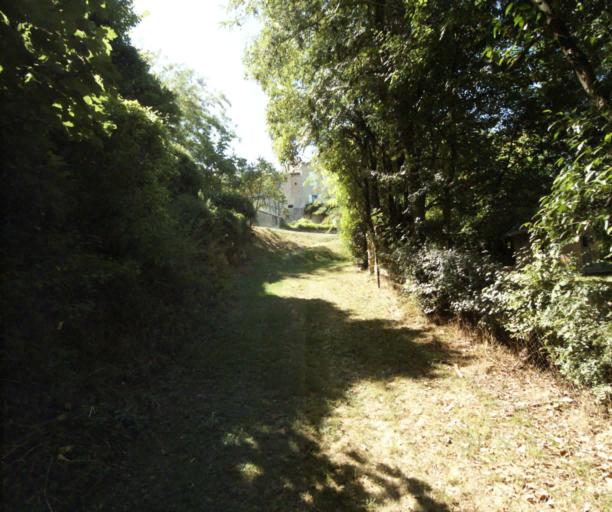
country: FR
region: Midi-Pyrenees
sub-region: Departement de la Haute-Garonne
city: Saint-Felix-Lauragais
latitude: 43.4894
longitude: 1.8991
